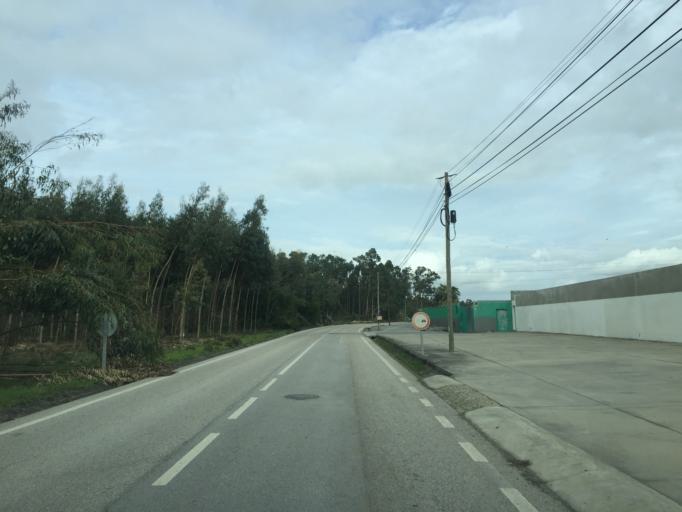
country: PT
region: Coimbra
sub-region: Figueira da Foz
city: Lavos
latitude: 40.0436
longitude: -8.8183
